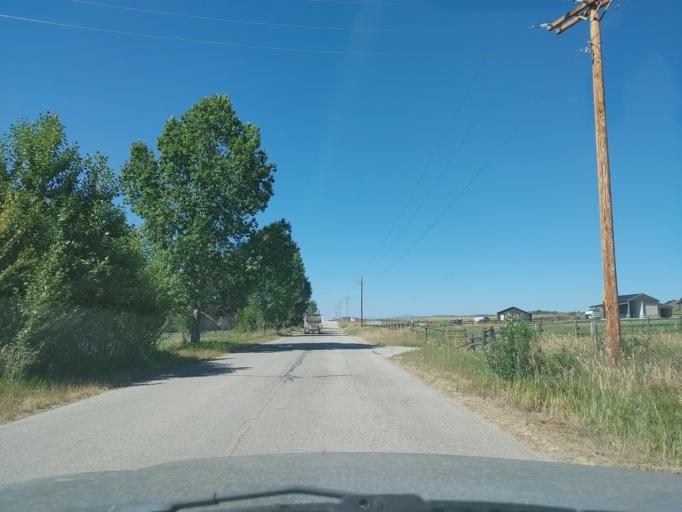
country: US
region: Montana
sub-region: Ravalli County
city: Hamilton
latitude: 46.3471
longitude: -114.0615
